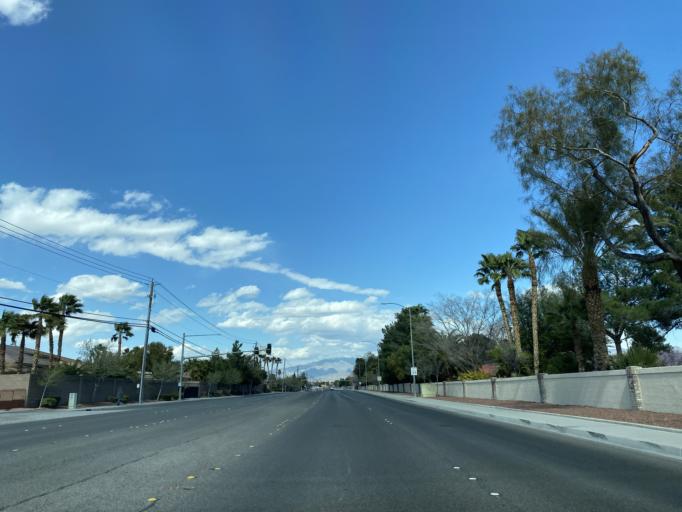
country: US
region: Nevada
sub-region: Clark County
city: Spring Valley
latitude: 36.2447
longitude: -115.2603
